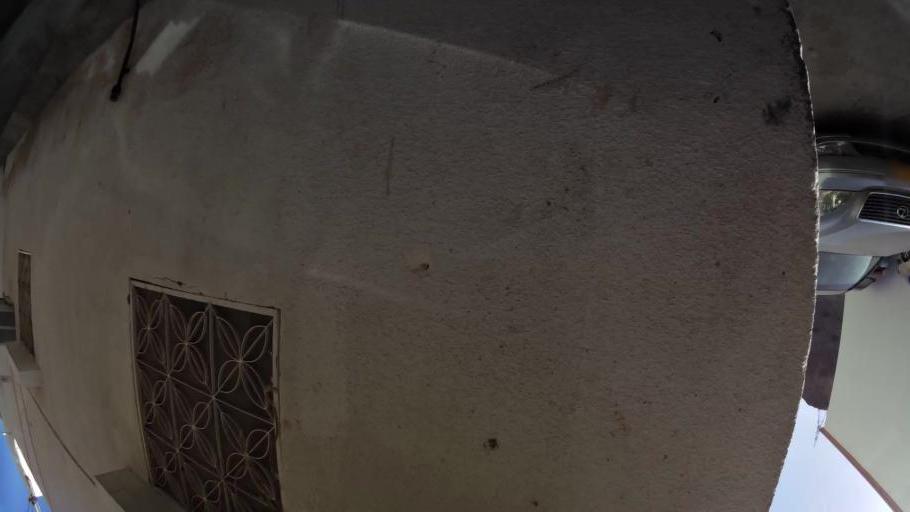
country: OM
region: Muhafazat Masqat
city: Muscat
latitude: 23.5846
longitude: 58.5145
